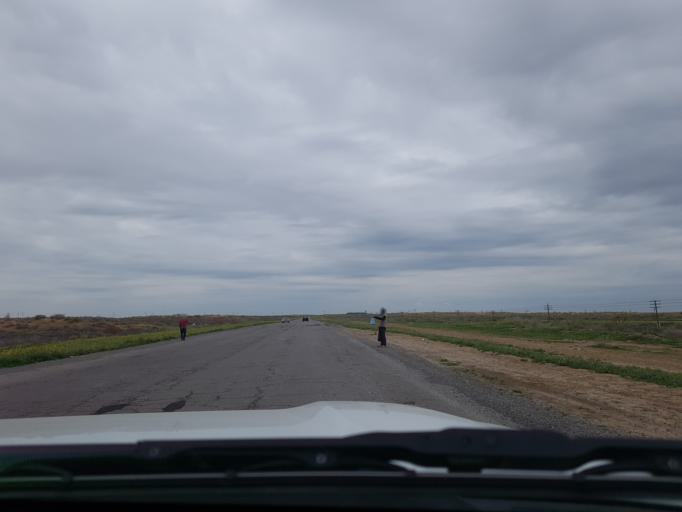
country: TM
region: Mary
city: Bayramaly
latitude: 37.7233
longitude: 62.4405
